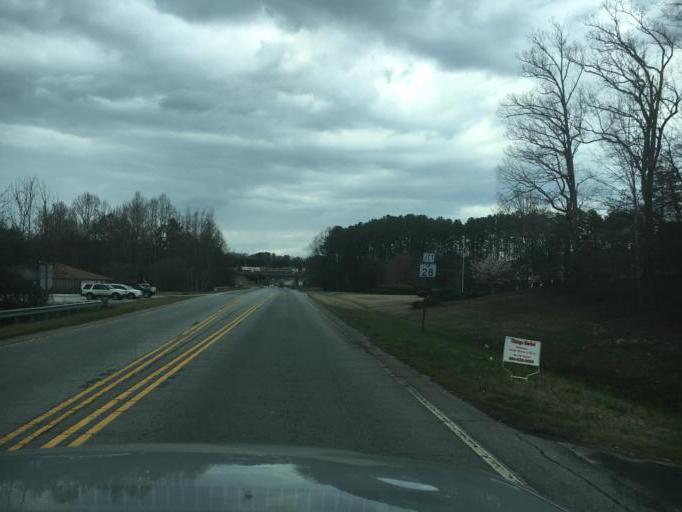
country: US
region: South Carolina
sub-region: Oconee County
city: Walhalla
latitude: 34.7501
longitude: -83.0482
